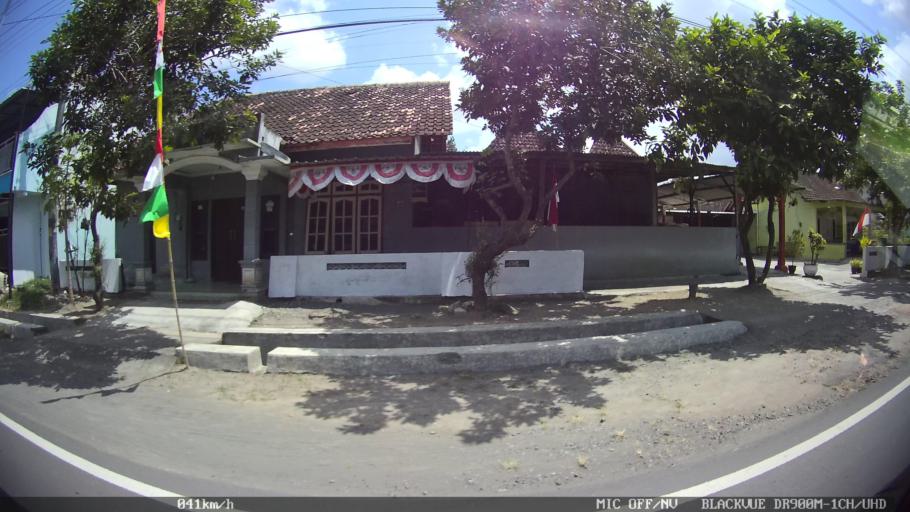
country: ID
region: Daerah Istimewa Yogyakarta
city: Bantul
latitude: -7.9059
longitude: 110.3450
